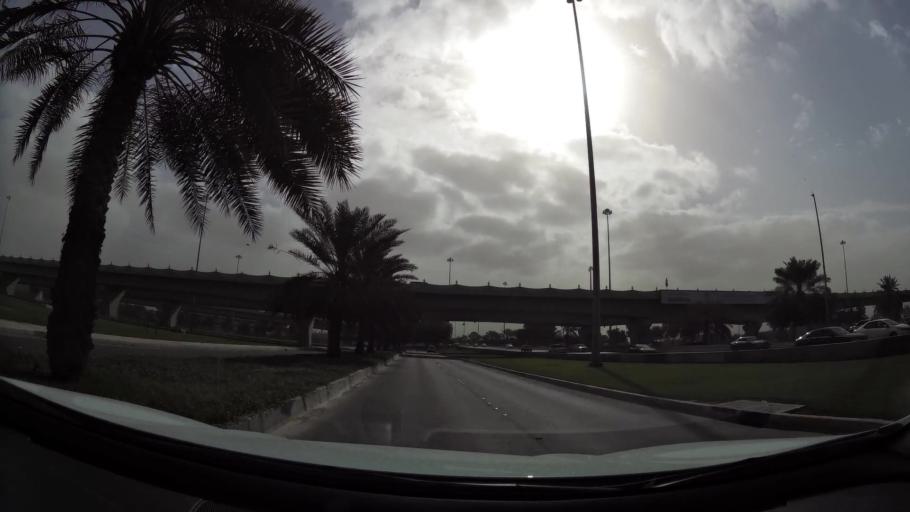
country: AE
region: Abu Dhabi
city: Abu Dhabi
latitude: 24.4064
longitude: 54.4769
